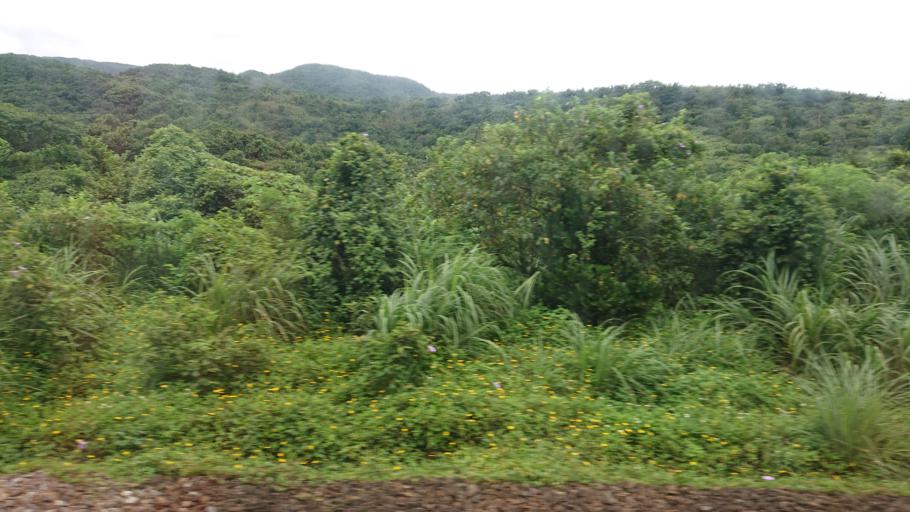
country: TW
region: Taiwan
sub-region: Keelung
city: Keelung
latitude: 25.0096
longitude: 121.9544
